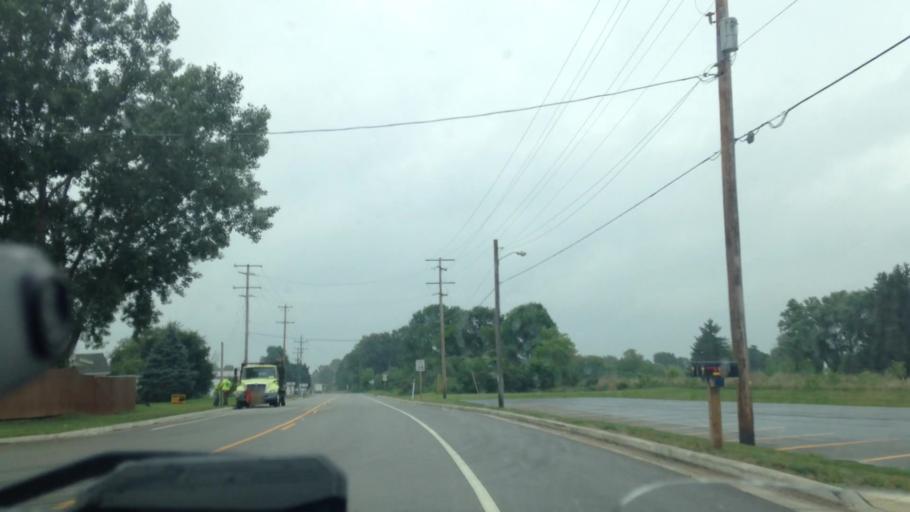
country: US
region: Wisconsin
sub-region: Washington County
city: Slinger
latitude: 43.3099
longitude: -88.2581
